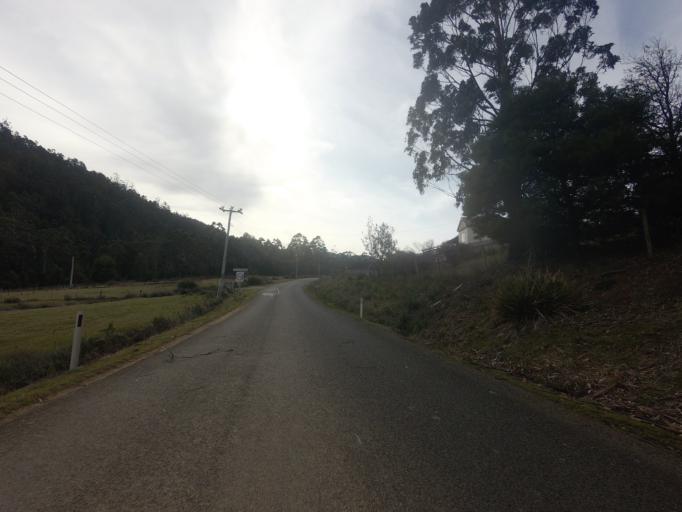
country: AU
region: Tasmania
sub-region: Huon Valley
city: Huonville
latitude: -43.0516
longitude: 147.1072
